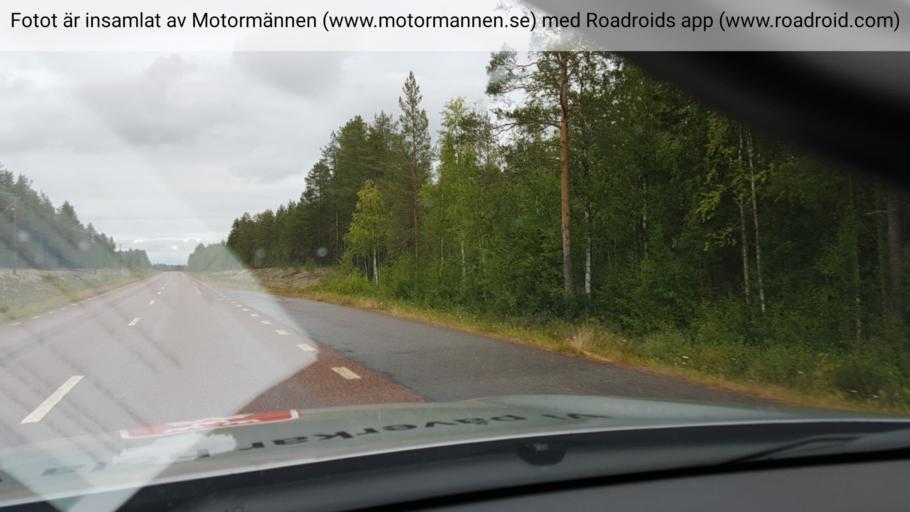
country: SE
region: Norrbotten
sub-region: Pajala Kommun
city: Pajala
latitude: 67.1199
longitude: 22.6054
